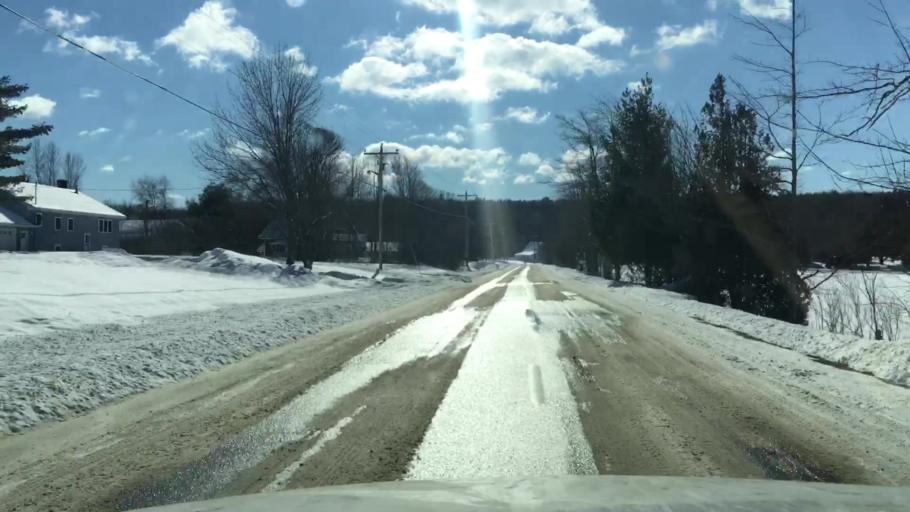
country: US
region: Maine
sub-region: Washington County
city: Calais
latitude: 45.0655
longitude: -67.4725
